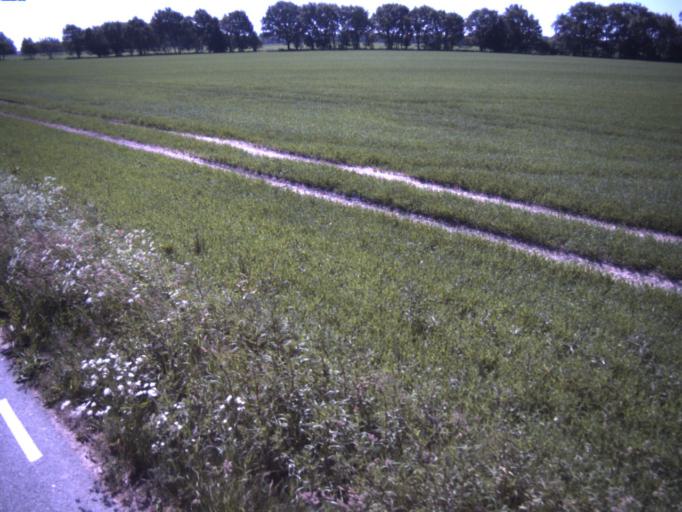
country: SE
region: Skane
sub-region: Helsingborg
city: Odakra
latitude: 56.1115
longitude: 12.6775
